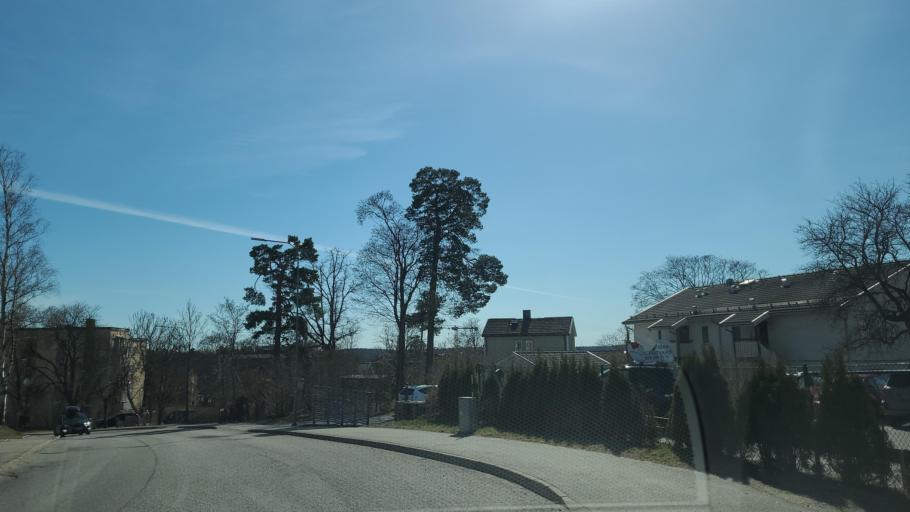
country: SE
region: Stockholm
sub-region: Lidingo
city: Brevik
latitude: 59.3180
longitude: 18.2294
